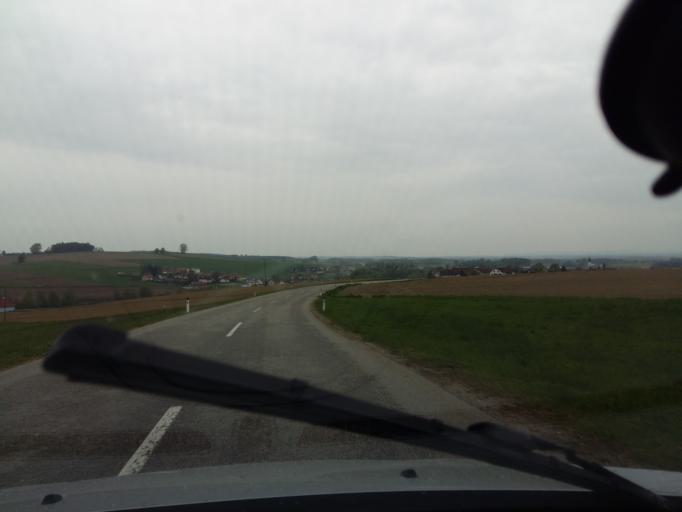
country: AT
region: Upper Austria
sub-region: Politischer Bezirk Scharding
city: Sankt Marienkirchen bei Schaerding
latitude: 48.3912
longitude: 13.4663
